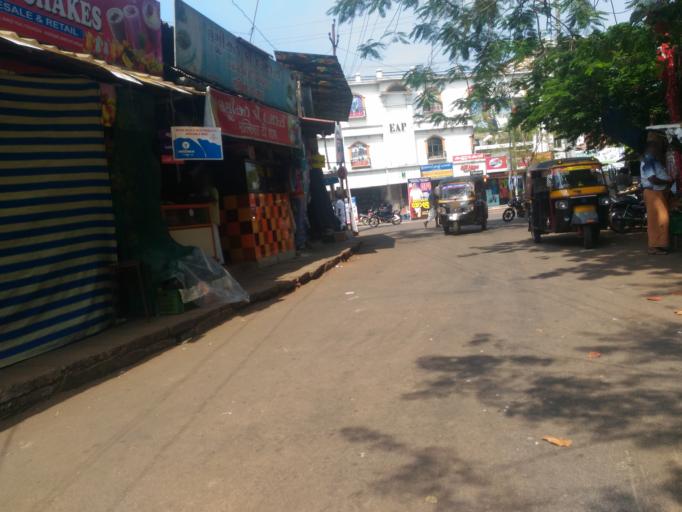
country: IN
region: Kerala
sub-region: Ernakulam
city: Muvattupula
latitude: 9.8966
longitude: 76.7112
